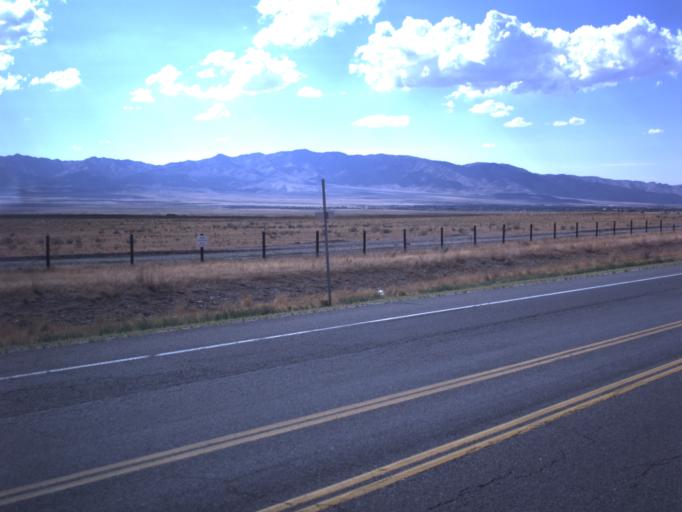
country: US
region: Utah
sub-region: Tooele County
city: Tooele
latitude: 40.5506
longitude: -112.3440
